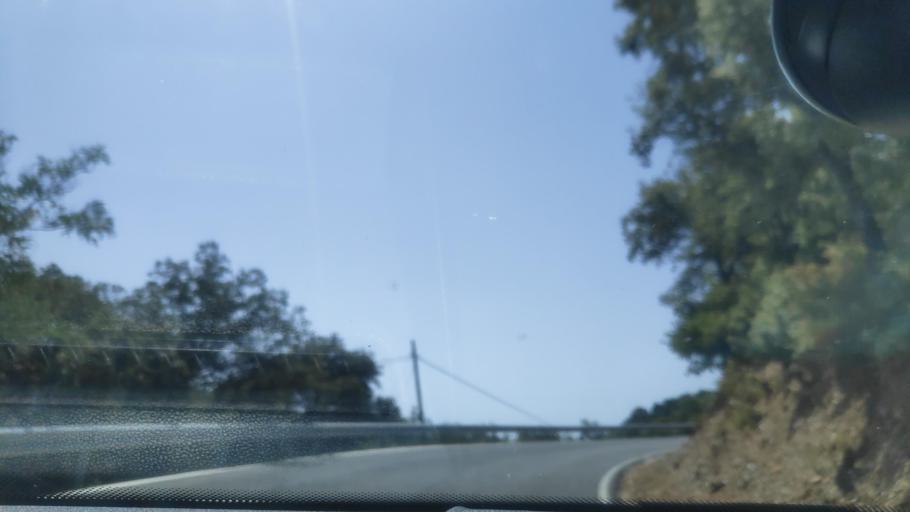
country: ES
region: Andalusia
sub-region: Provincia de Granada
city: Trevelez
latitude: 36.9765
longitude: -3.2781
